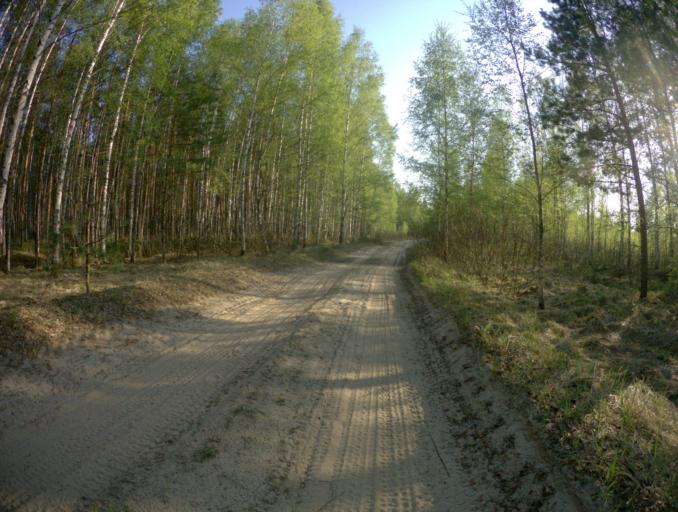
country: RU
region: Vladimir
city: Vyazniki
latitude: 56.3759
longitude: 42.1724
